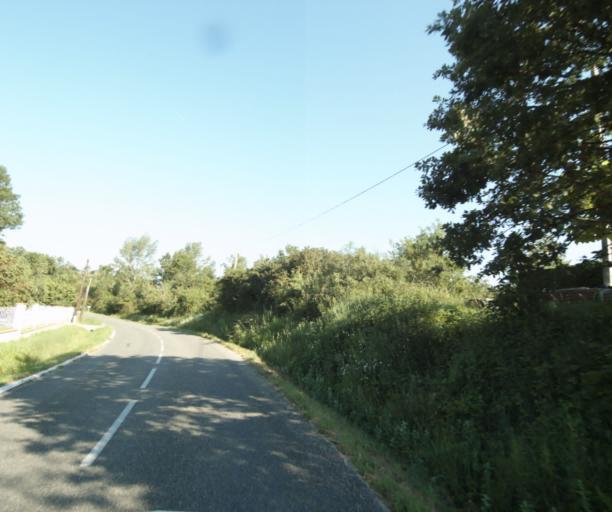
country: FR
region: Midi-Pyrenees
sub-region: Departement du Tarn-et-Garonne
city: Saint-Nauphary
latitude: 44.0172
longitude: 1.4204
